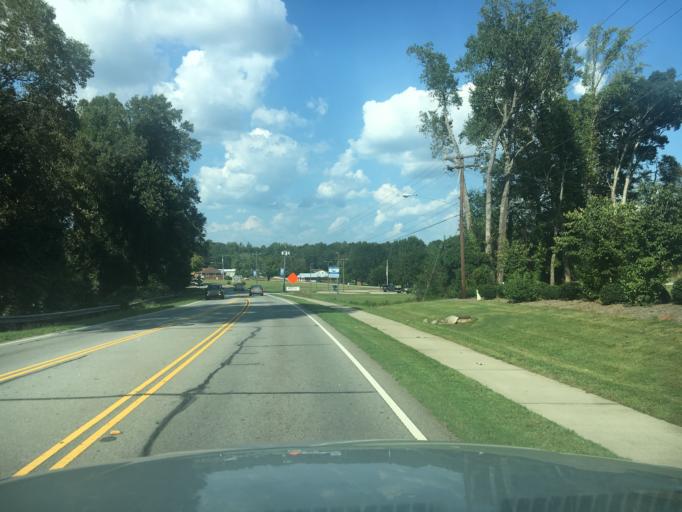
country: US
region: South Carolina
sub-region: Anderson County
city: Pendleton
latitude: 34.6387
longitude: -82.7822
